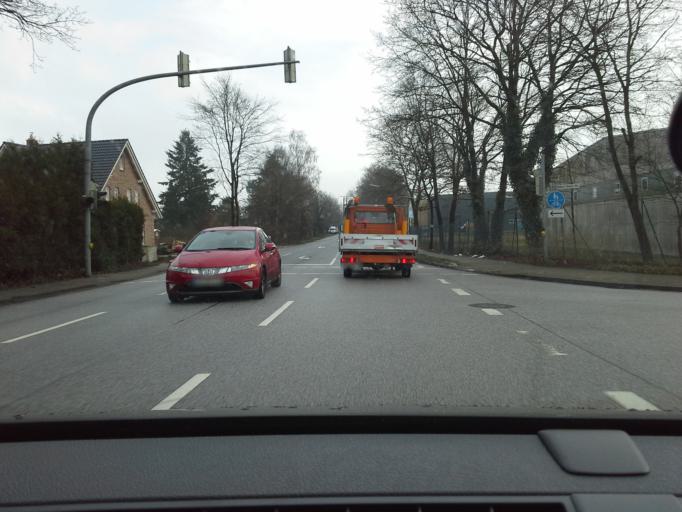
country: DE
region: Schleswig-Holstein
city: Ellerau
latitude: 53.7483
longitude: 9.9376
